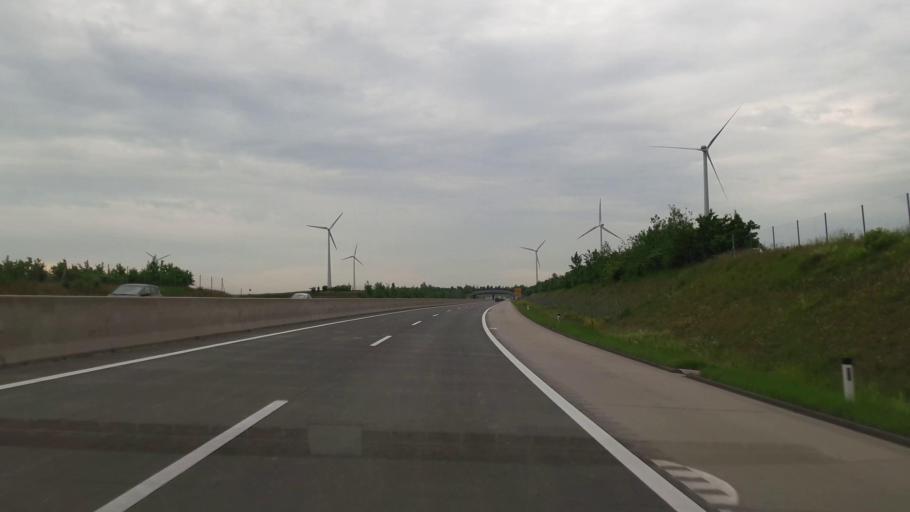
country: AT
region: Burgenland
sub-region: Politischer Bezirk Neusiedl am See
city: Potzneusiedl
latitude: 48.0384
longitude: 16.9085
